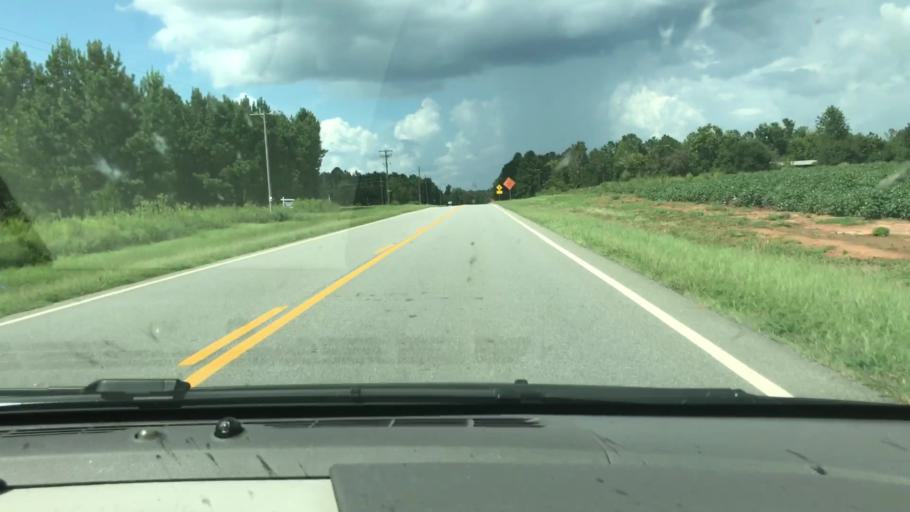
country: US
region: Georgia
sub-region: Quitman County
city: Georgetown
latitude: 31.8122
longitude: -85.0935
